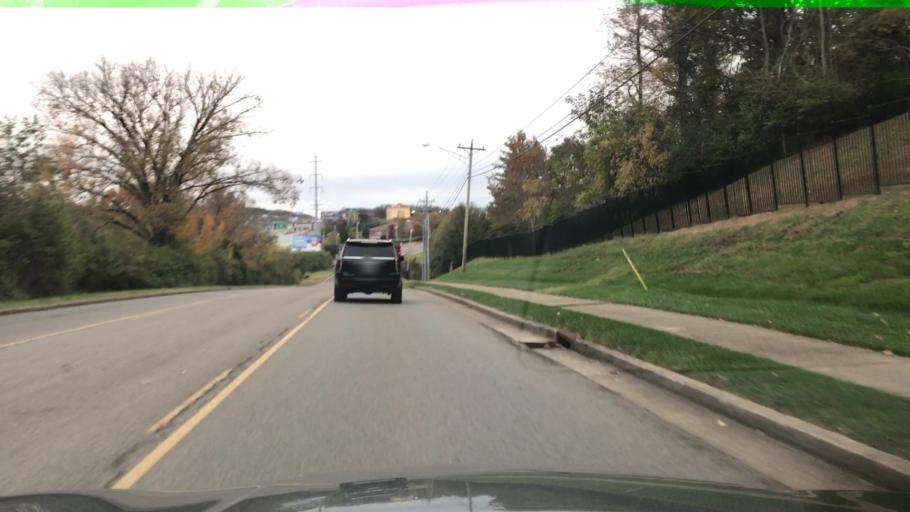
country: US
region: Tennessee
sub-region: Williamson County
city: Franklin
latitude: 35.9056
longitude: -86.8246
